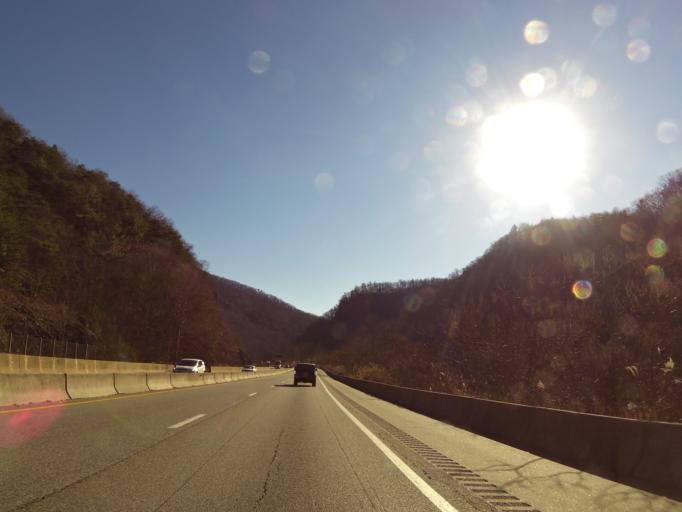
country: US
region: North Carolina
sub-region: Haywood County
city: Cove Creek
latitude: 35.7735
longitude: -83.0915
